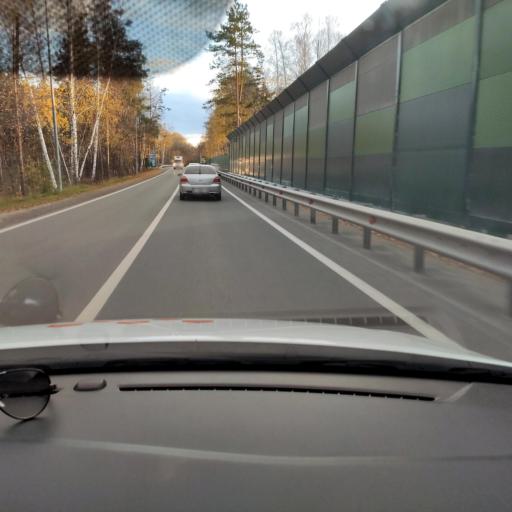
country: RU
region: Tatarstan
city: Verkhniy Uslon
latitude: 55.6272
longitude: 49.0140
